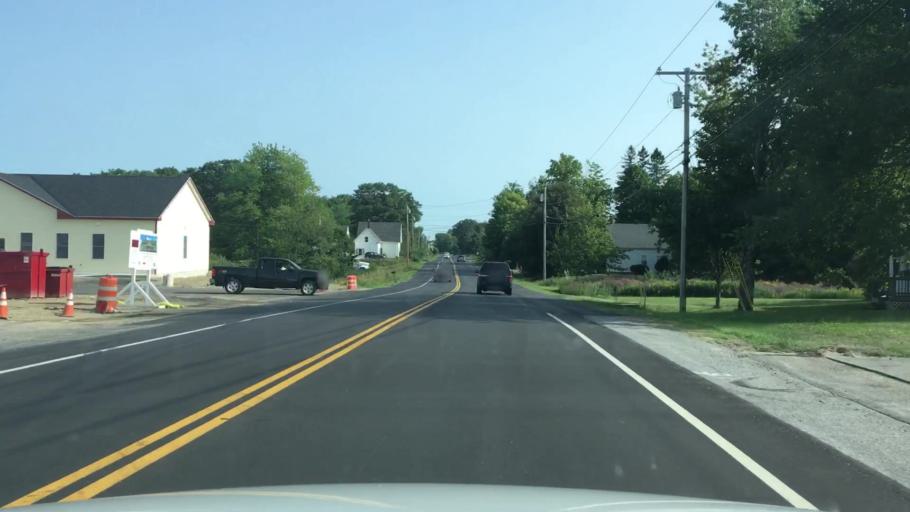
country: US
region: Maine
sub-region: Knox County
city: Warren
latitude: 44.1117
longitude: -69.2545
